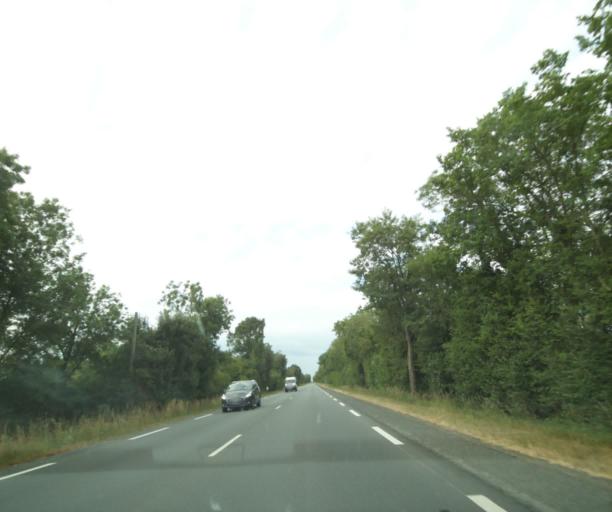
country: FR
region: Poitou-Charentes
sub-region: Departement de la Charente-Maritime
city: Andilly
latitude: 46.2689
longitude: -1.0051
